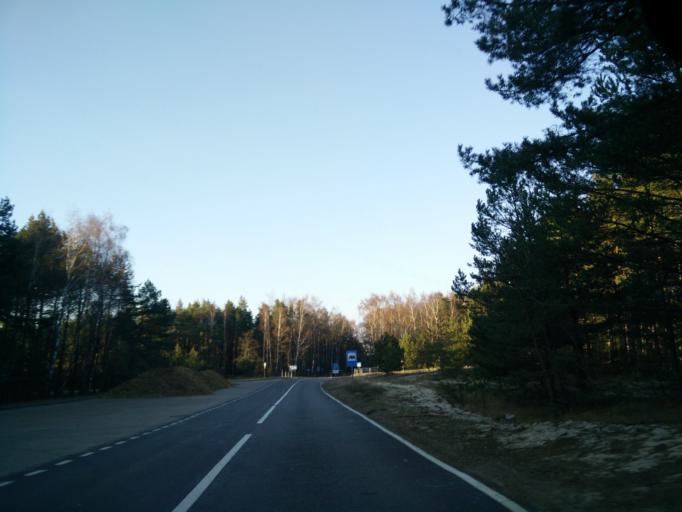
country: LT
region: Klaipedos apskritis
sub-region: Klaipeda
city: Klaipeda
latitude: 55.6780
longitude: 21.1131
